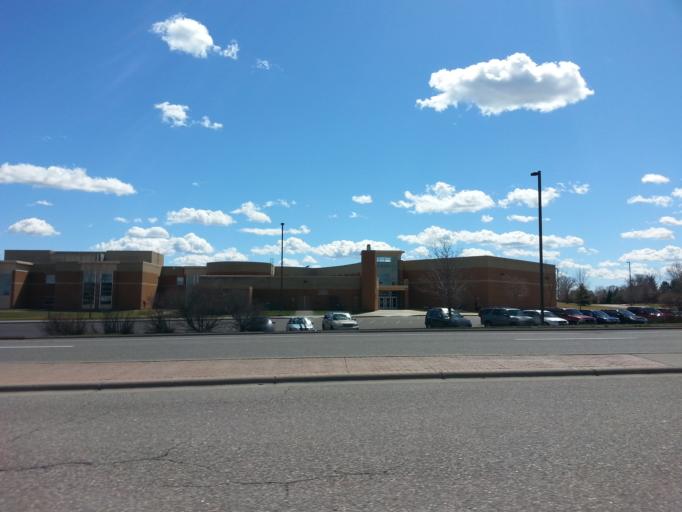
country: US
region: Minnesota
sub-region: Dakota County
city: Lakeville
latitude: 44.6814
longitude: -93.2561
